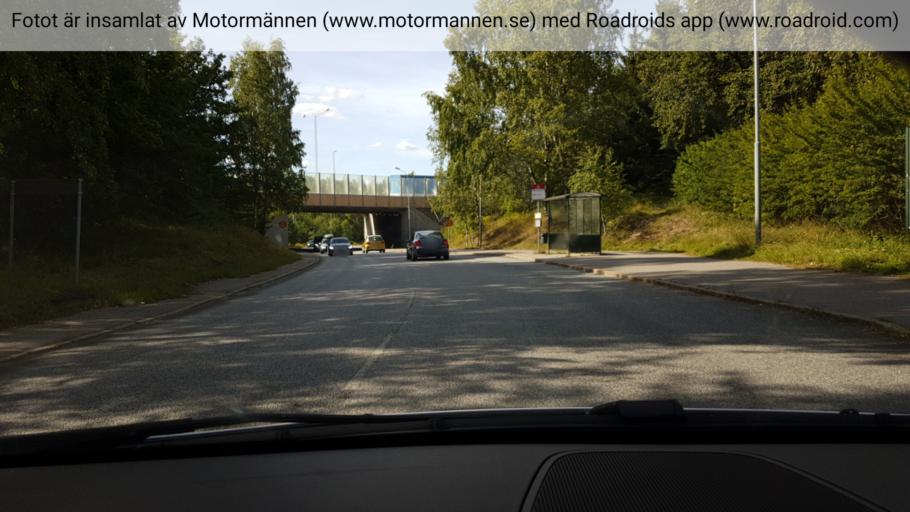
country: SE
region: Stockholm
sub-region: Sodertalje Kommun
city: Pershagen
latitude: 59.1553
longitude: 17.6466
